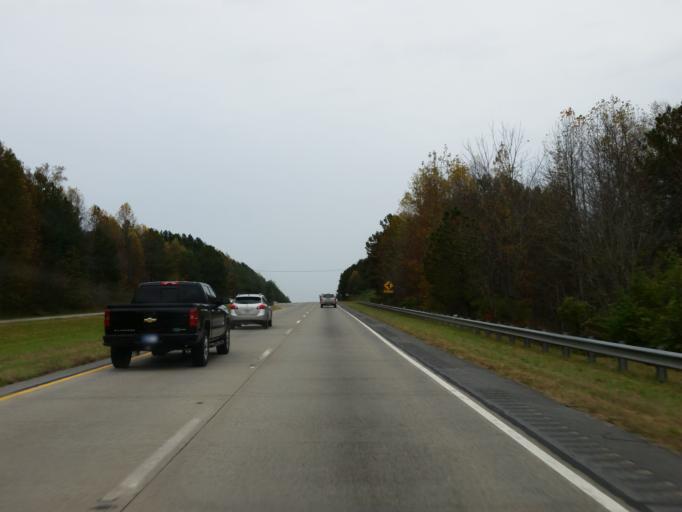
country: US
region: Georgia
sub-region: Pickens County
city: Jasper
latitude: 34.4190
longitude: -84.4294
